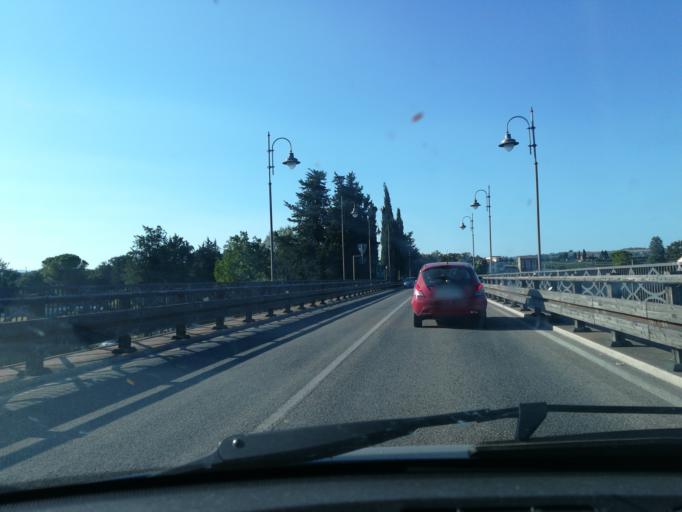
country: IT
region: The Marches
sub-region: Provincia di Macerata
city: Villa Potenza
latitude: 43.3270
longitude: 13.4263
